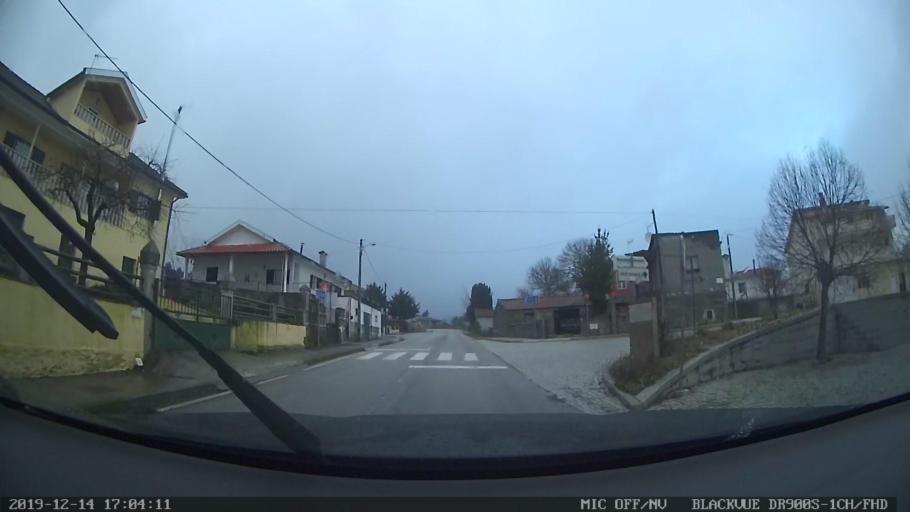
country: PT
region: Vila Real
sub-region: Vila Pouca de Aguiar
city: Vila Pouca de Aguiar
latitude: 41.4463
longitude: -7.5725
